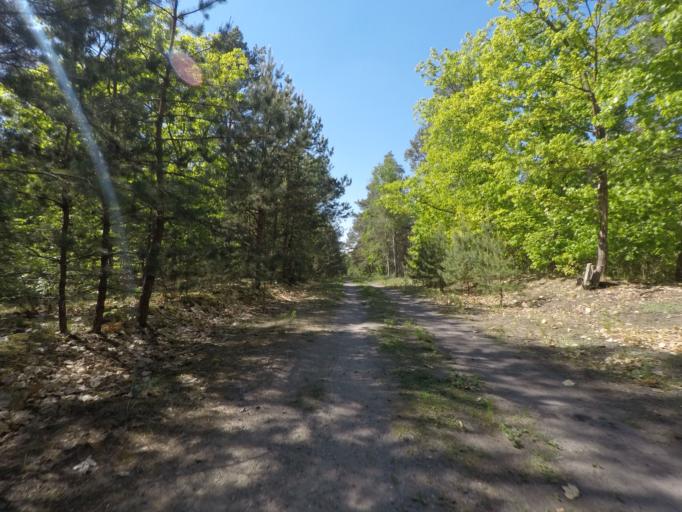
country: DE
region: Brandenburg
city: Eberswalde
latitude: 52.8144
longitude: 13.7692
